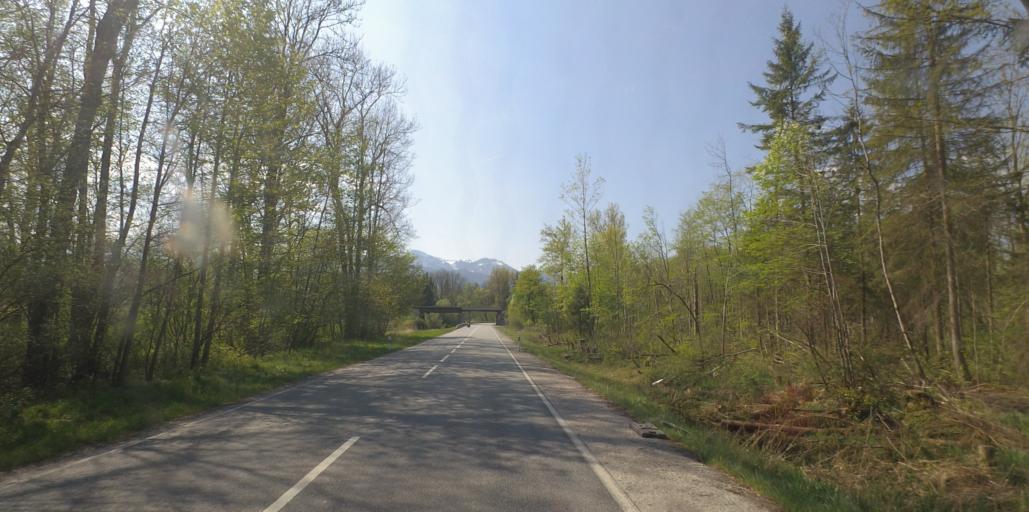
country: DE
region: Bavaria
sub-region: Upper Bavaria
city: Ubersee
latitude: 47.8233
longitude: 12.5110
